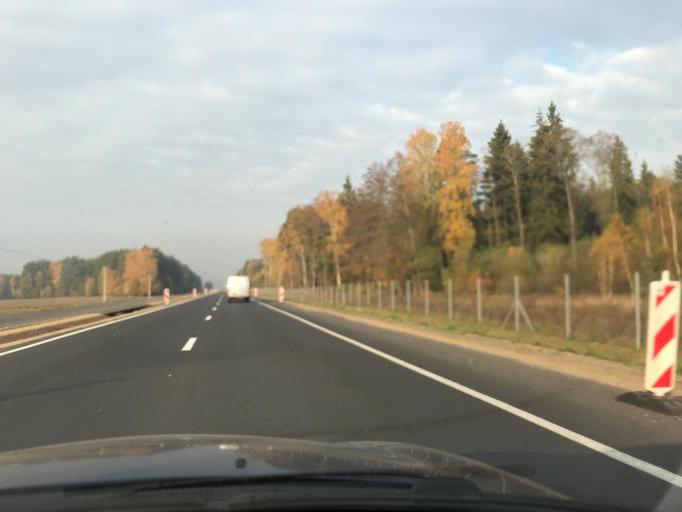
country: BY
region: Grodnenskaya
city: Lida
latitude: 53.8291
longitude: 25.3950
